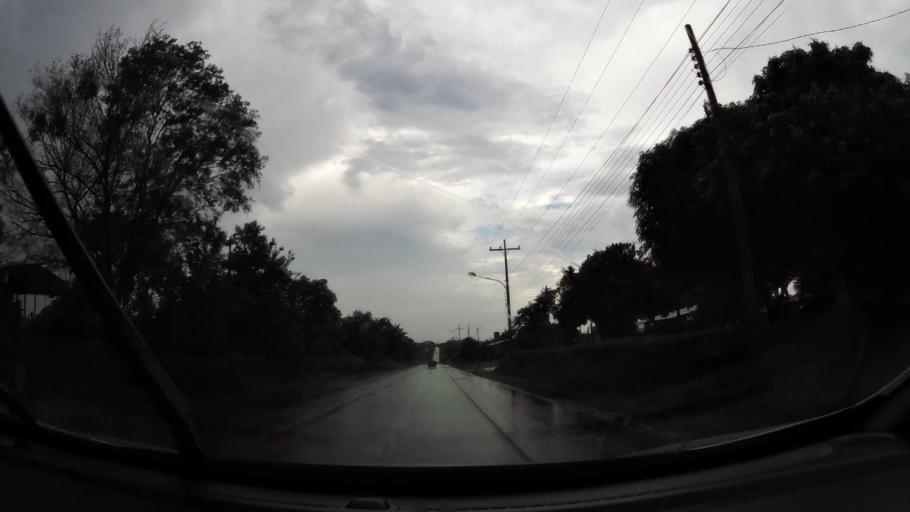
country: PY
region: Alto Parana
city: Presidente Franco
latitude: -25.5591
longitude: -54.6618
